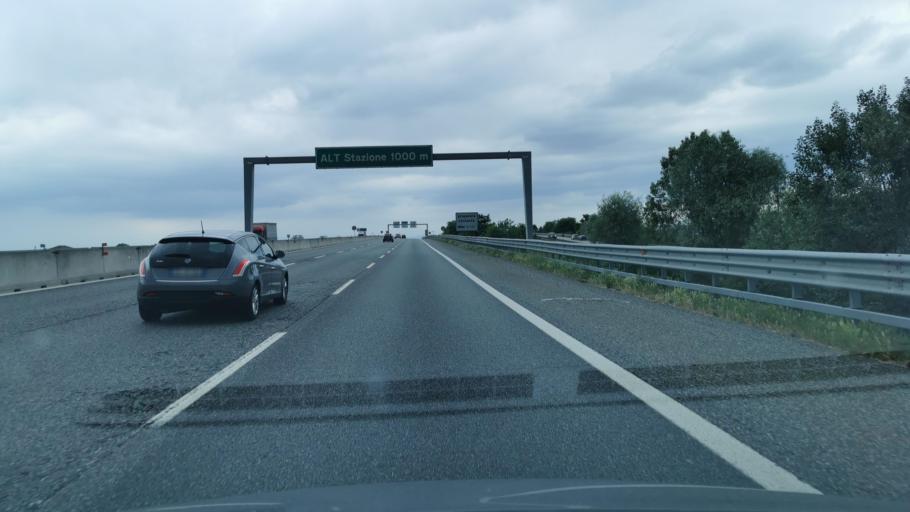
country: IT
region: Piedmont
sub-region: Provincia di Torino
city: Trofarello
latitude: 44.9640
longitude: 7.7502
